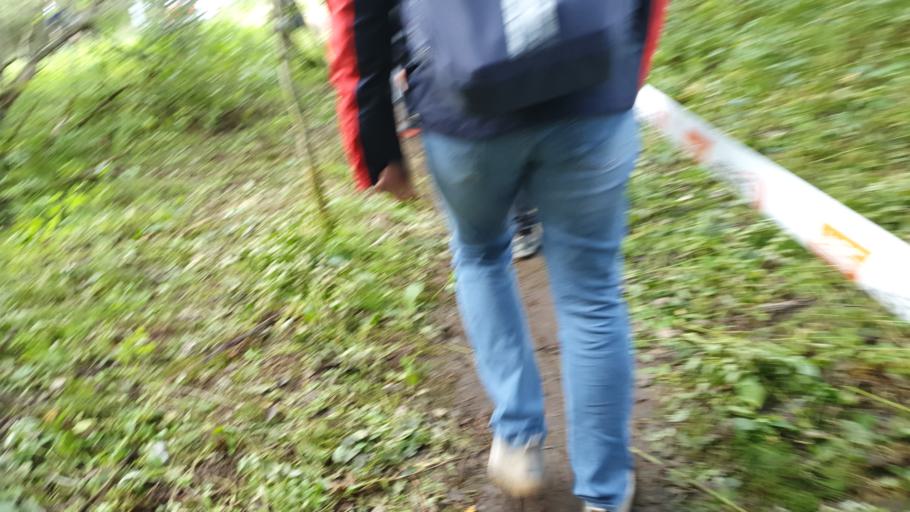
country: EE
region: Tartu
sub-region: UElenurme vald
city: Ulenurme
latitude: 58.1327
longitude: 26.7739
